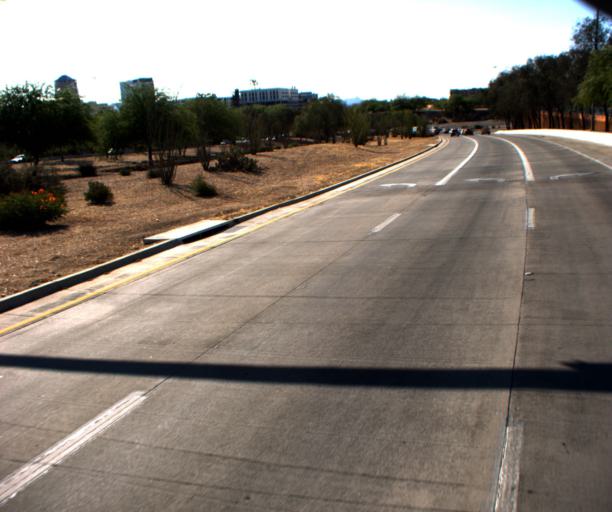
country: US
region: Arizona
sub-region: Pima County
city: South Tucson
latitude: 32.2193
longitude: -110.9601
